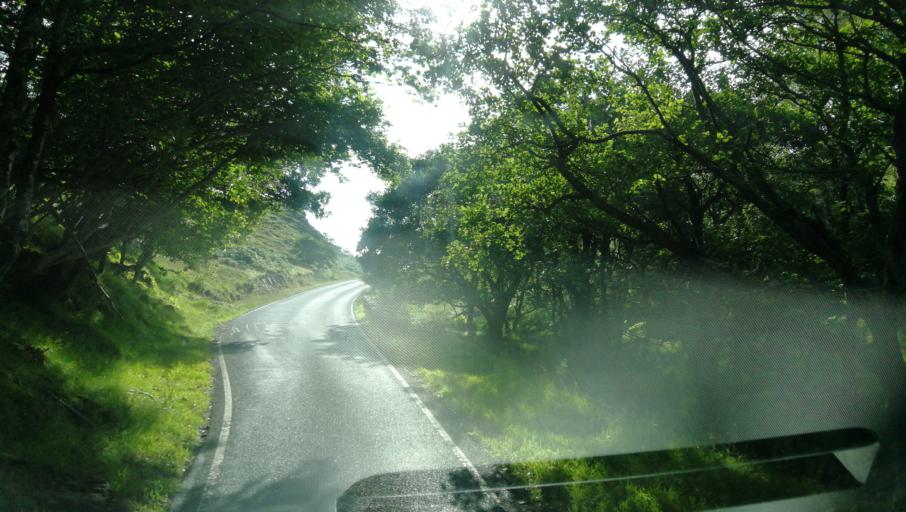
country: GB
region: Scotland
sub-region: Argyll and Bute
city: Isle Of Mull
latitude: 56.6797
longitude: -5.8536
